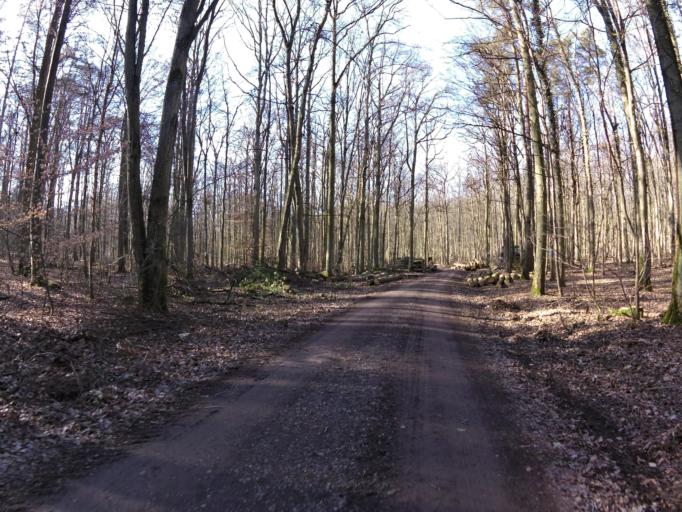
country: DE
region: Bavaria
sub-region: Regierungsbezirk Unterfranken
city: Estenfeld
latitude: 49.8551
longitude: 9.9935
